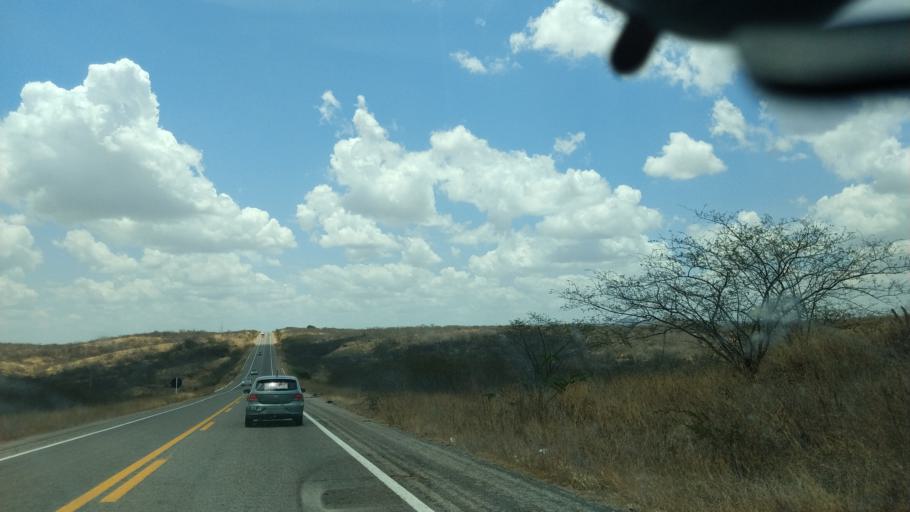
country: BR
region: Rio Grande do Norte
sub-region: Cerro Cora
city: Cerro Cora
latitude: -6.2020
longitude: -36.3330
